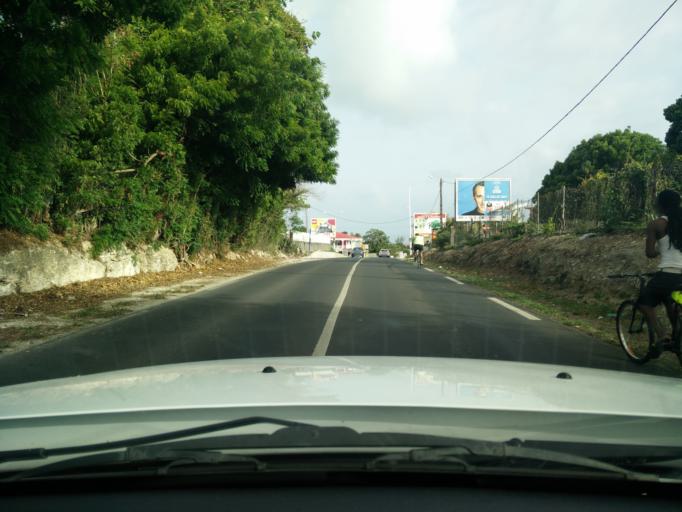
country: GP
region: Guadeloupe
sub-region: Guadeloupe
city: Saint-Francois
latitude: 16.2571
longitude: -61.2900
